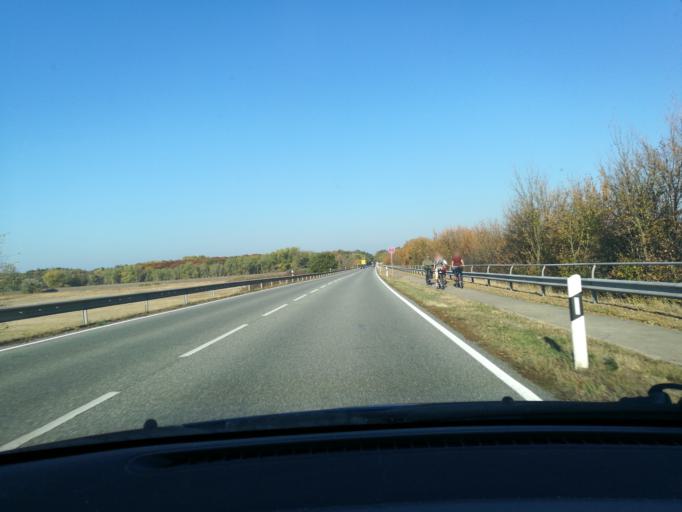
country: DE
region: Mecklenburg-Vorpommern
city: Domitz
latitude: 53.1458
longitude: 11.2303
